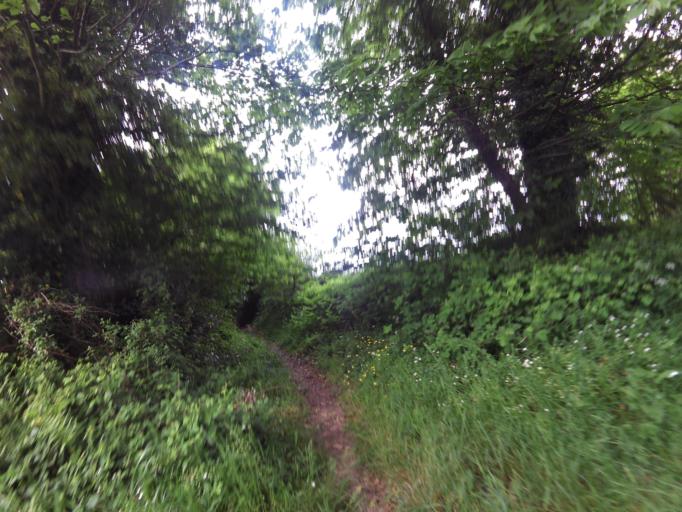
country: FR
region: Brittany
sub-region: Departement du Morbihan
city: Molac
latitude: 47.7671
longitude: -2.4307
